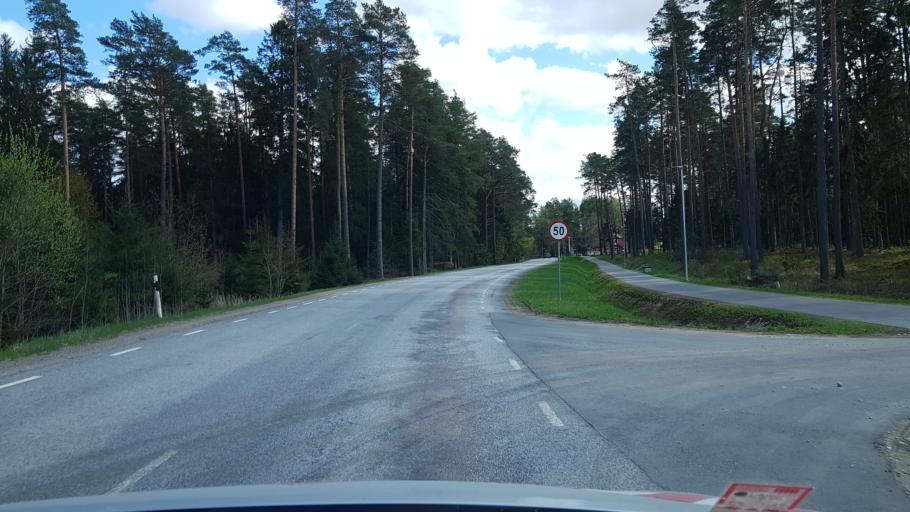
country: EE
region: Tartu
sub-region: UElenurme vald
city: Ulenurme
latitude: 58.3189
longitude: 26.8333
